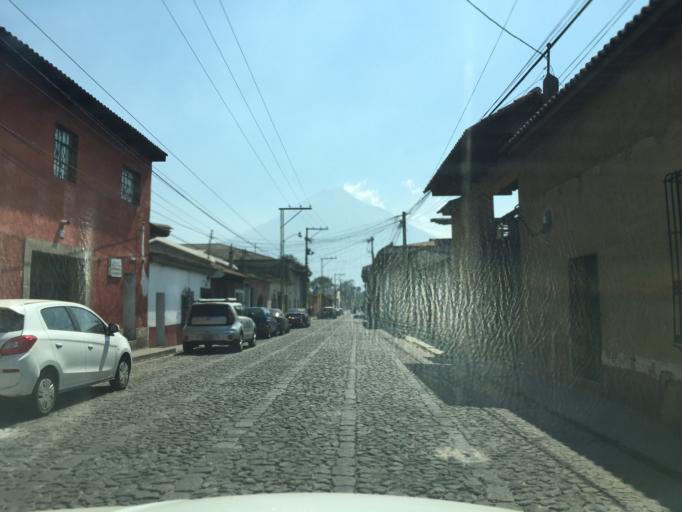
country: GT
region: Sacatepequez
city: Antigua Guatemala
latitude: 14.5656
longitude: -90.7392
